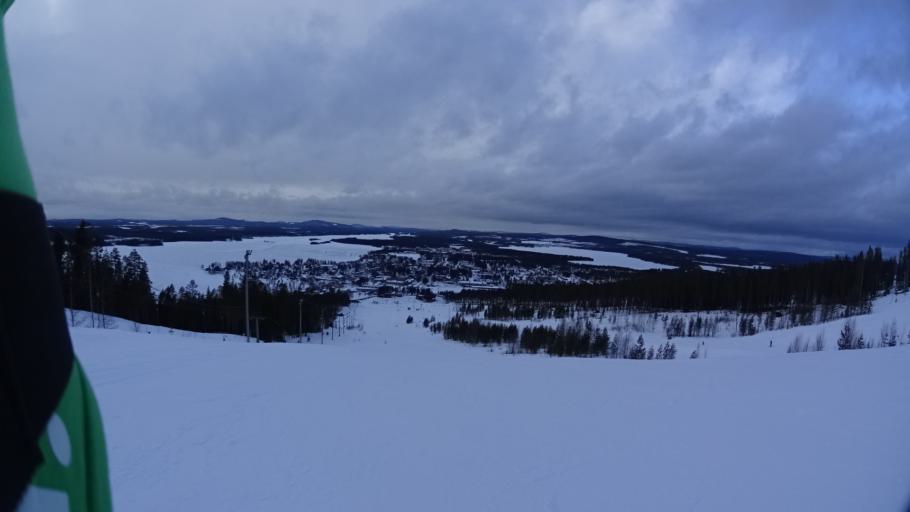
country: SE
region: Vaesterbotten
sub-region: Mala Kommun
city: Mala
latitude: 65.1774
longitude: 18.7619
